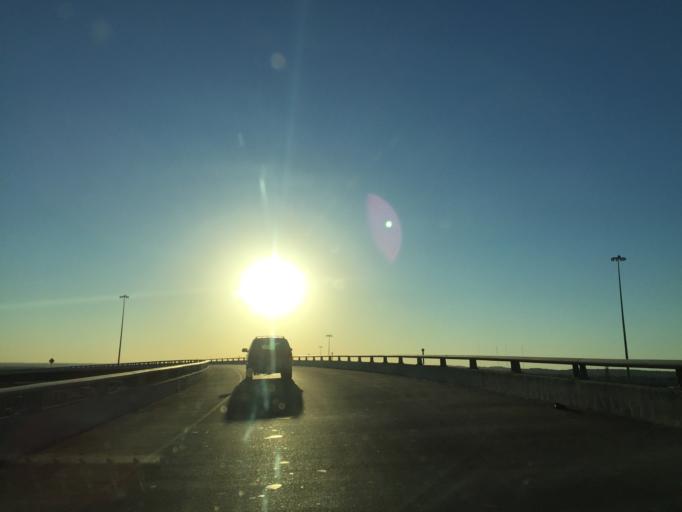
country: US
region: Texas
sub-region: Travis County
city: Austin
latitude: 30.3226
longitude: -97.7056
